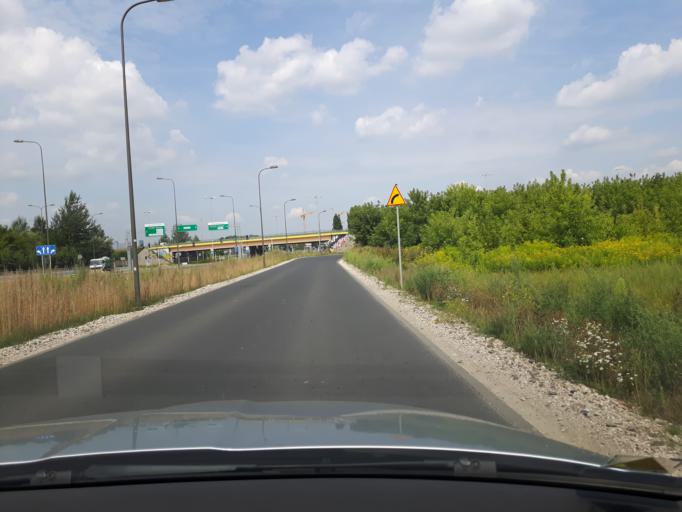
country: PL
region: Masovian Voivodeship
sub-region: Warszawa
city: Mokotow
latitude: 52.2017
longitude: 21.0705
